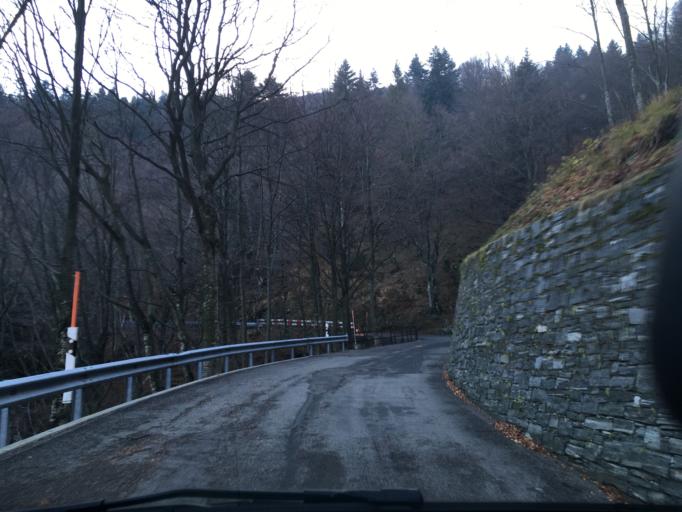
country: CH
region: Ticino
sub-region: Locarno District
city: Magadino
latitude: 46.1141
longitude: 8.8476
